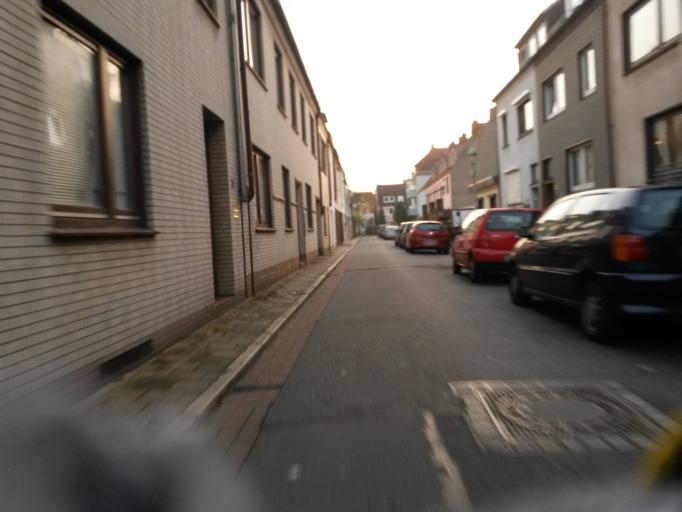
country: DE
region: Bremen
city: Bremen
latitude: 53.0654
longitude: 8.8719
